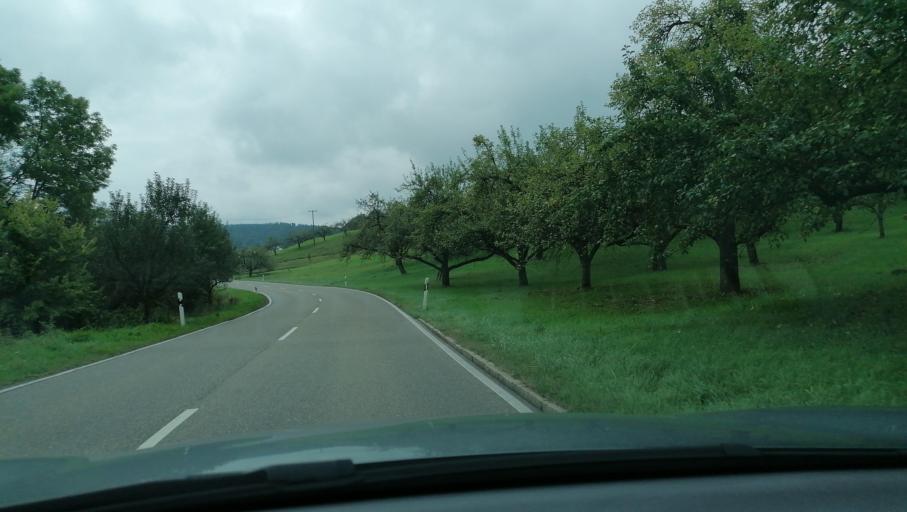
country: DE
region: Baden-Wuerttemberg
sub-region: Regierungsbezirk Stuttgart
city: Winnenden
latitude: 48.8535
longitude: 9.4414
